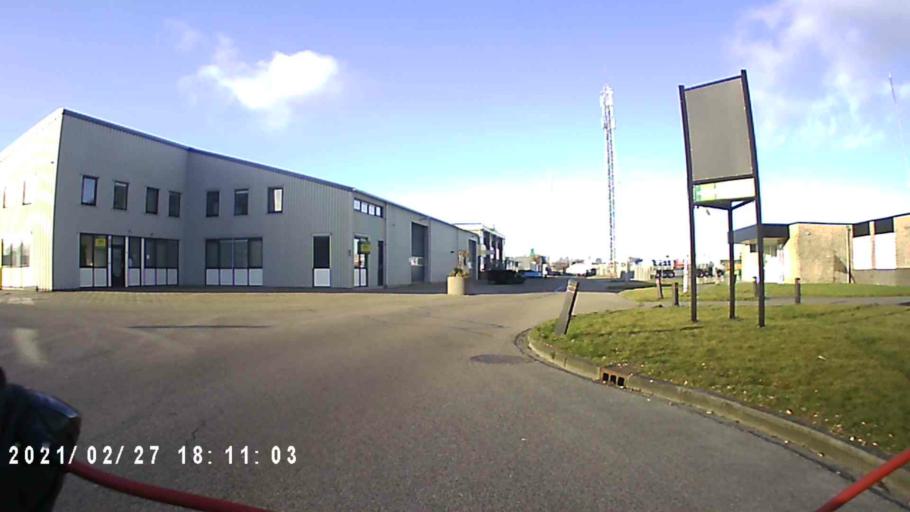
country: NL
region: Groningen
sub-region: Gemeente Bedum
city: Bedum
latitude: 53.2945
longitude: 6.5956
